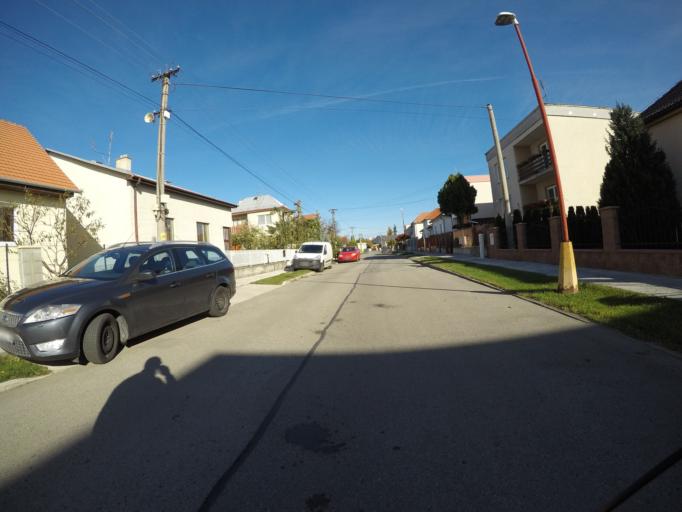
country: SK
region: Trenciansky
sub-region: Okres Nove Mesto nad Vahom
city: Nove Mesto nad Vahom
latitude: 48.7474
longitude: 17.8293
